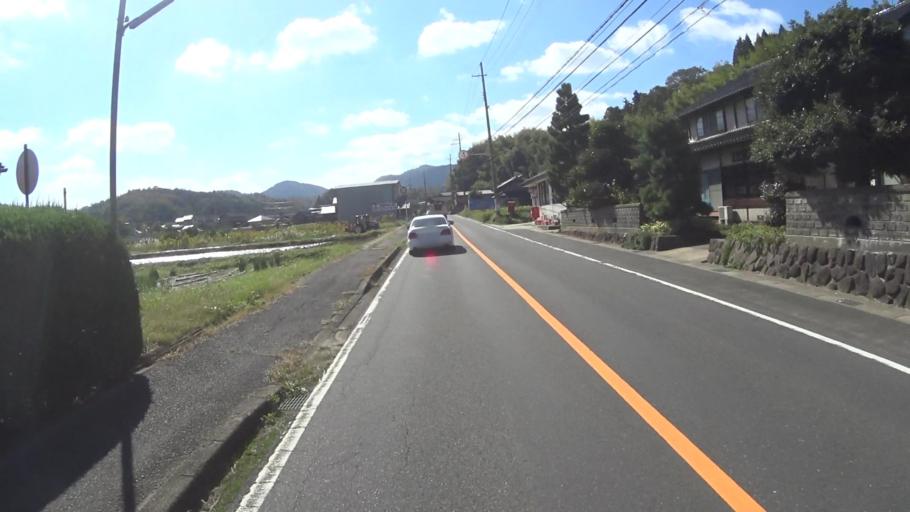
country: JP
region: Kyoto
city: Miyazu
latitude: 35.6550
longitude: 135.0326
